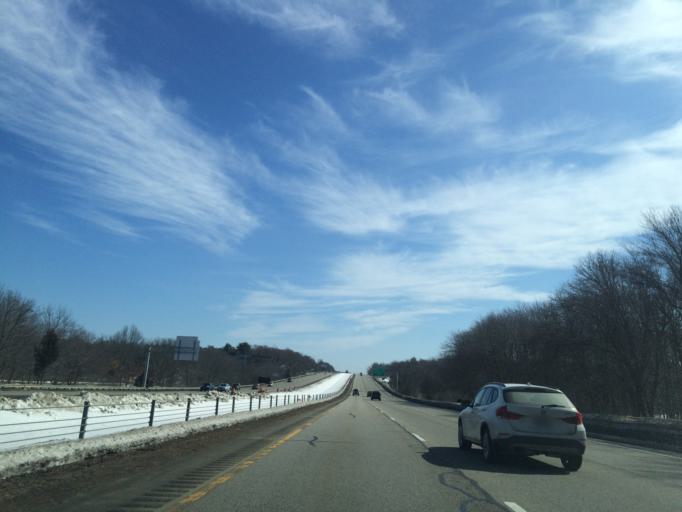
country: US
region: Massachusetts
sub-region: Middlesex County
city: Lexington
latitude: 42.4218
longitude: -71.2399
